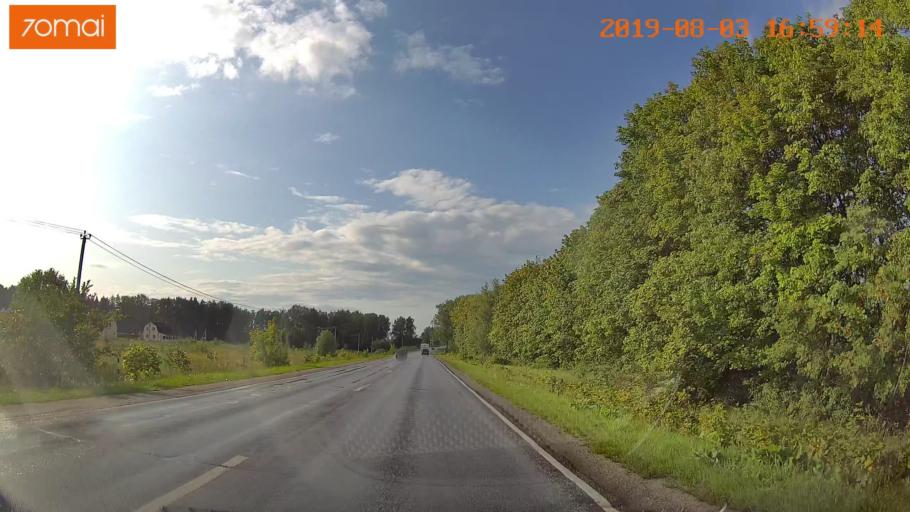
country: RU
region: Moskovskaya
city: Voskresensk
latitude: 55.3282
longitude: 38.6261
